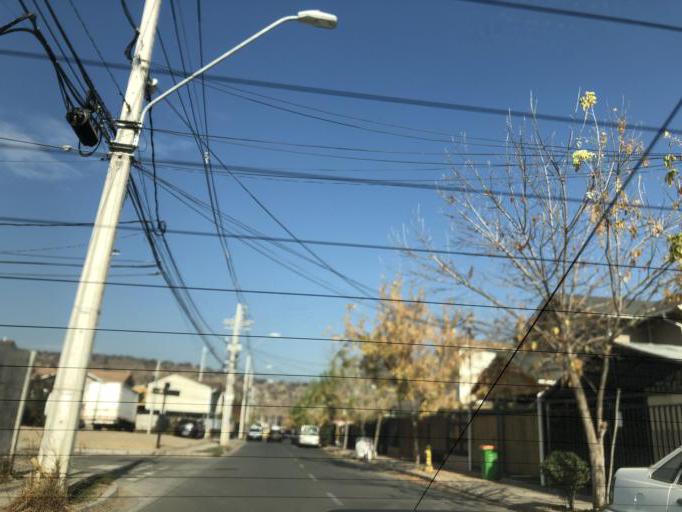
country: CL
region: Santiago Metropolitan
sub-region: Provincia de Cordillera
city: Puente Alto
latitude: -33.5973
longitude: -70.5484
